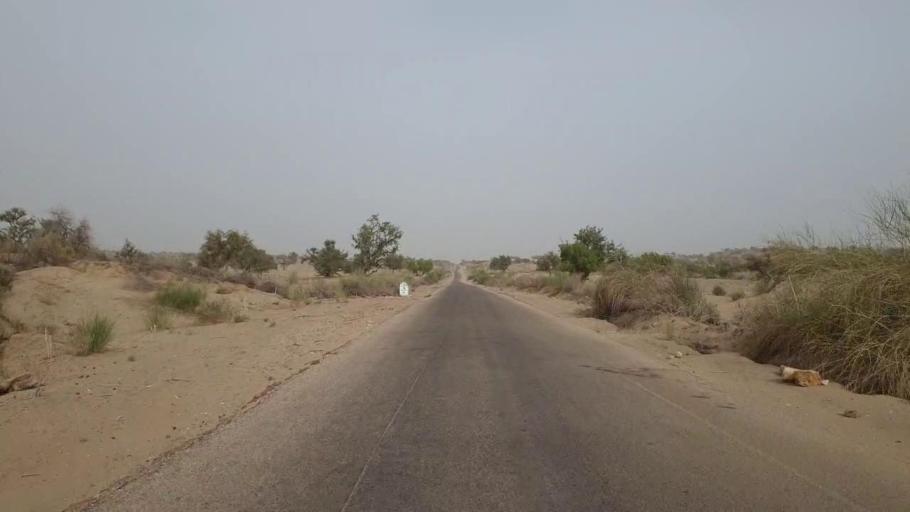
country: PK
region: Sindh
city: Islamkot
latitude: 24.5644
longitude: 70.3337
